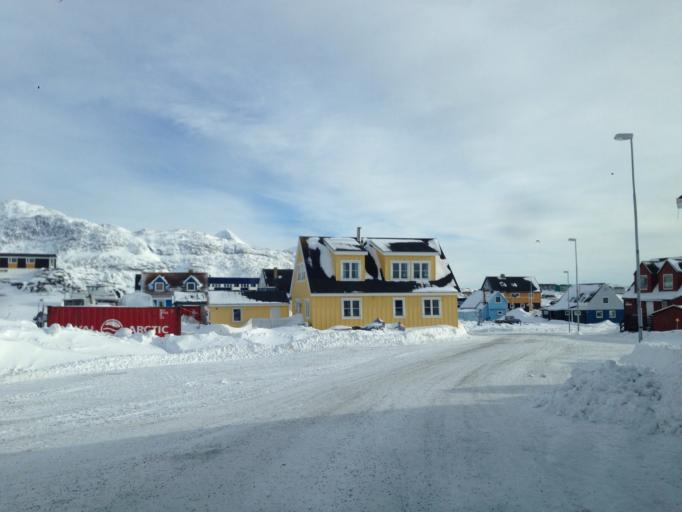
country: GL
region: Sermersooq
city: Nuuk
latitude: 64.1800
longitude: -51.7352
